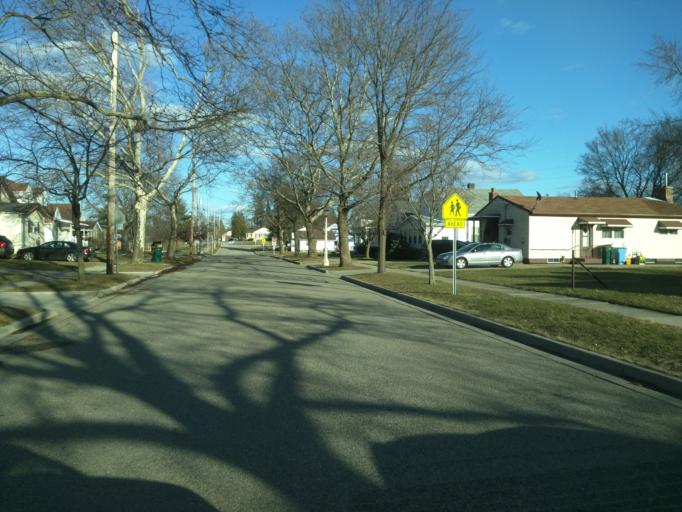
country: US
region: Michigan
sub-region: Ingham County
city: Lansing
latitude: 42.7589
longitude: -84.5493
